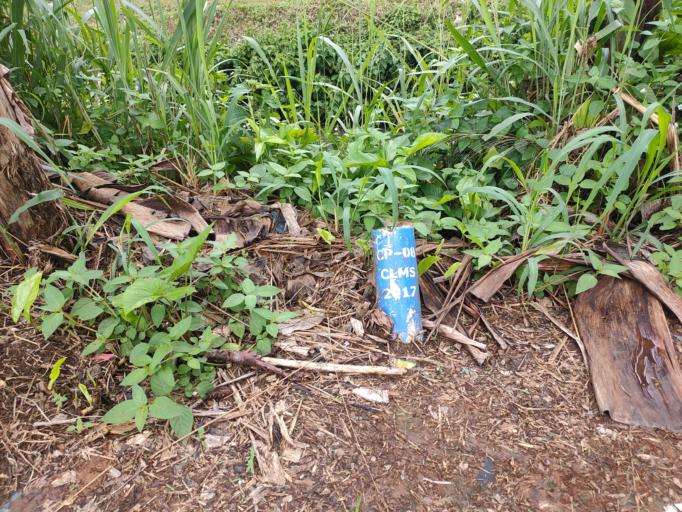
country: ID
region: West Java
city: Ciampea
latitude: -6.5240
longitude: 106.7031
